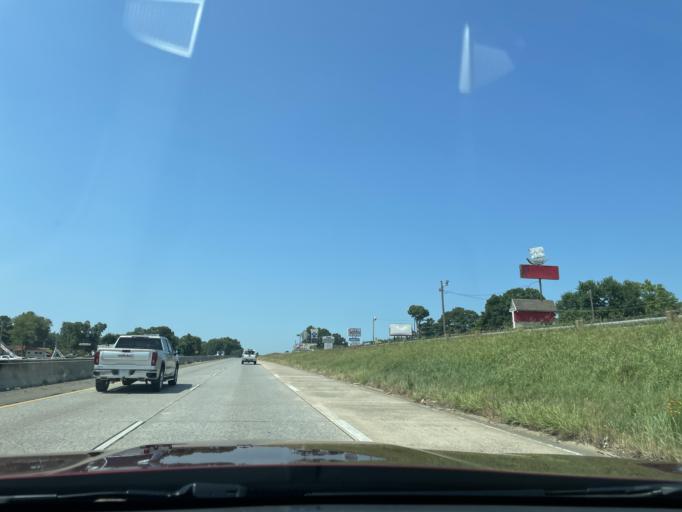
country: US
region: Arkansas
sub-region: Pulaski County
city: Jacksonville
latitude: 34.8798
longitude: -92.1138
